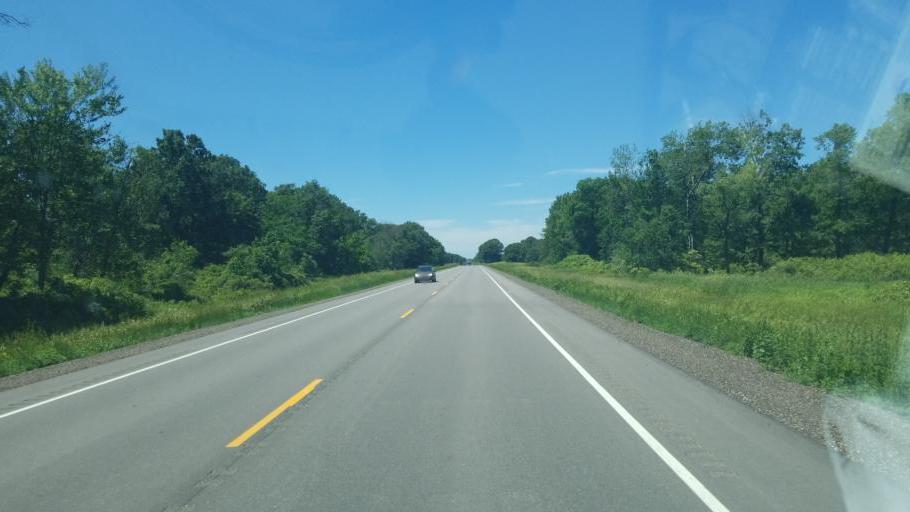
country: US
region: Wisconsin
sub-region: Juneau County
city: New Lisbon
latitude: 44.0258
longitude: -90.2630
